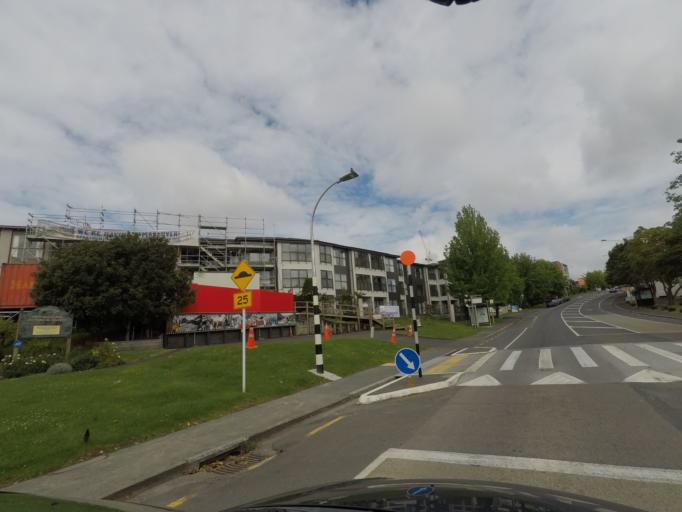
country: NZ
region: Auckland
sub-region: Auckland
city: Rosebank
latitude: -36.8762
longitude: 174.6323
